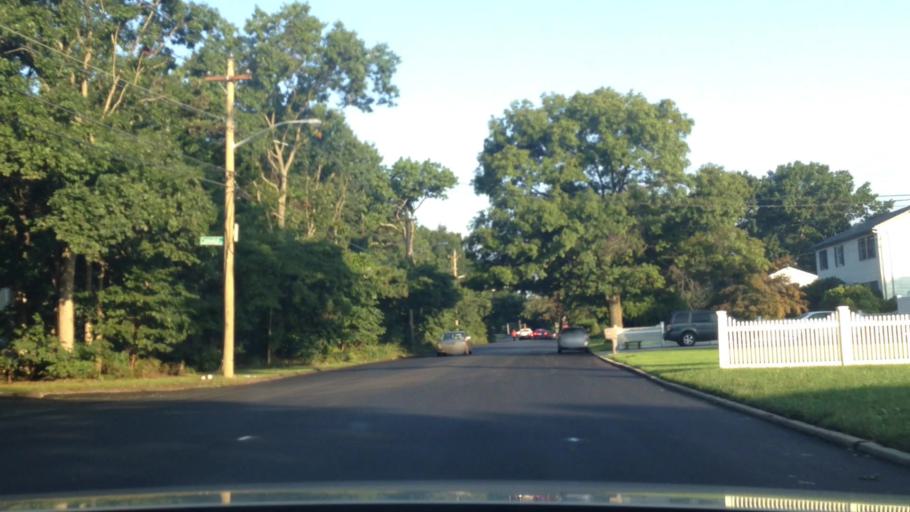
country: US
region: New York
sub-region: Suffolk County
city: Centereach
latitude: 40.8510
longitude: -73.0686
